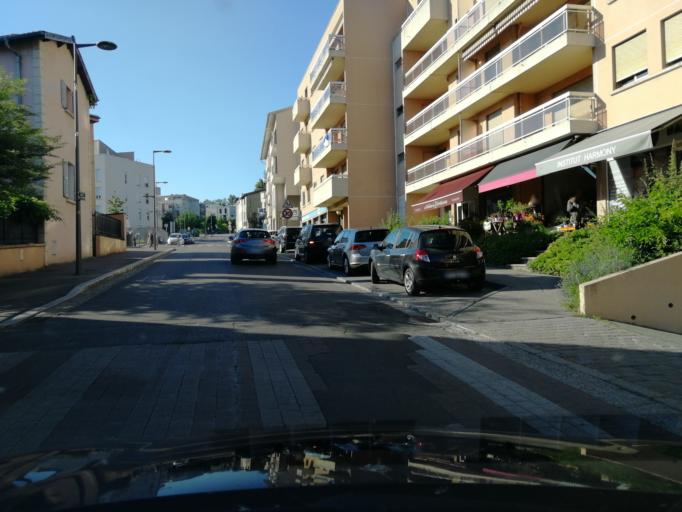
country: FR
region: Rhone-Alpes
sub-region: Departement du Rhone
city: Fontaines-sur-Saone
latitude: 45.8351
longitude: 4.8477
